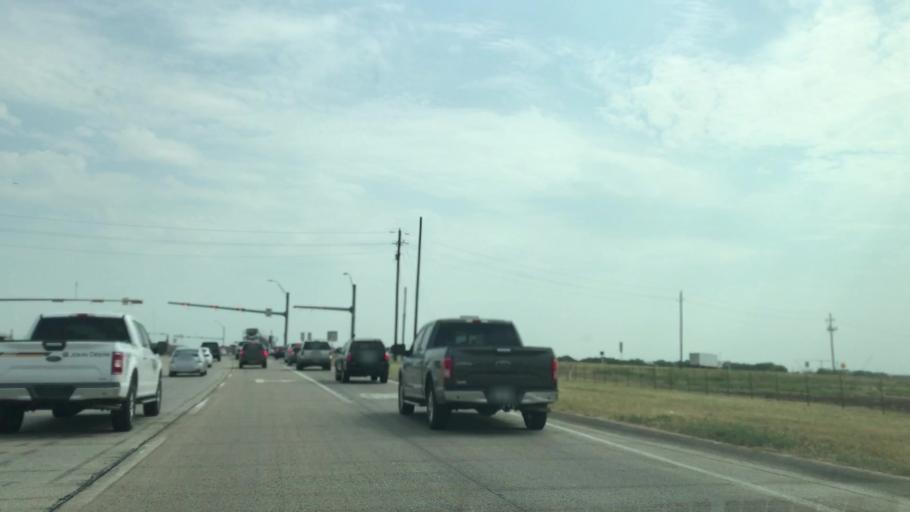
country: US
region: Texas
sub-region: Denton County
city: Roanoke
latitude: 32.9841
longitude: -97.2372
